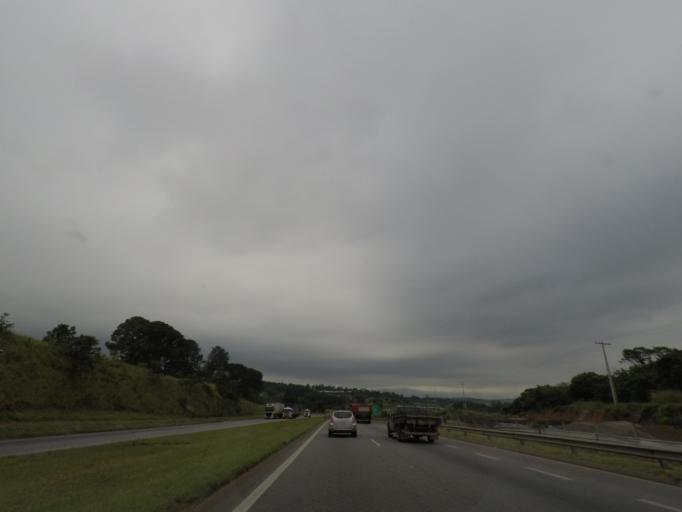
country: BR
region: Sao Paulo
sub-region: Jarinu
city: Jarinu
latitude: -23.0642
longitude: -46.6477
